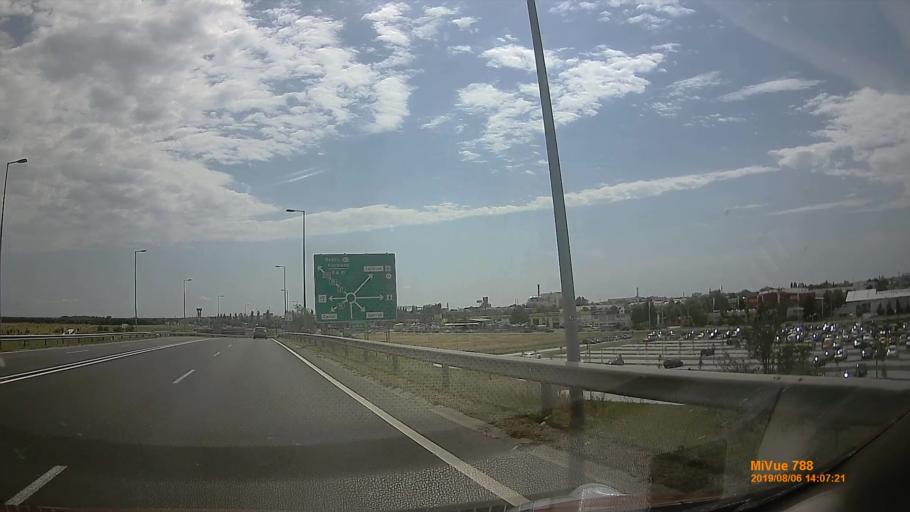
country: HU
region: Vas
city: Szombathely
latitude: 47.2448
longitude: 16.6549
